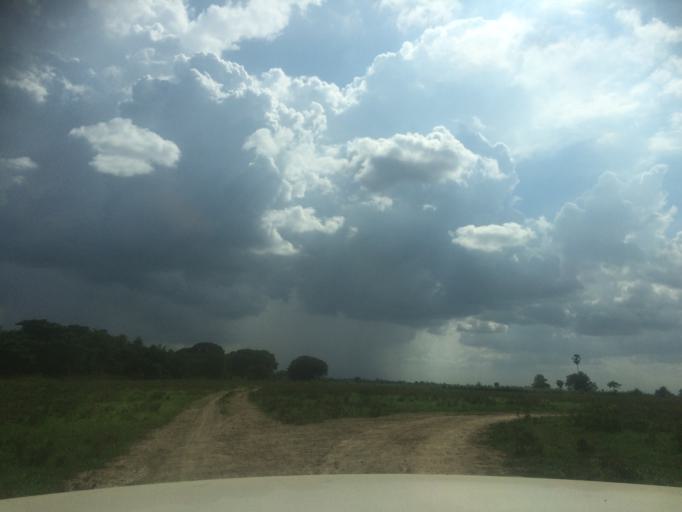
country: MM
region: Ayeyarwady
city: Hinthada
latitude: 17.7404
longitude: 95.3775
